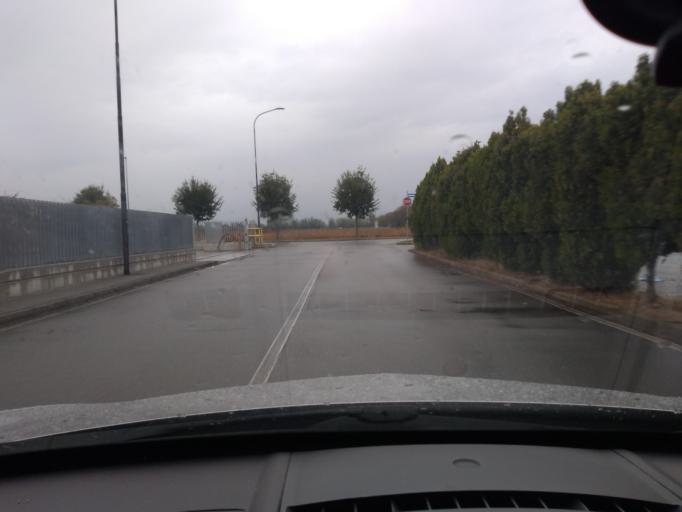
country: IT
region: Lombardy
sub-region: Provincia di Bergamo
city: Mornico al Serio
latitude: 45.5912
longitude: 9.7905
